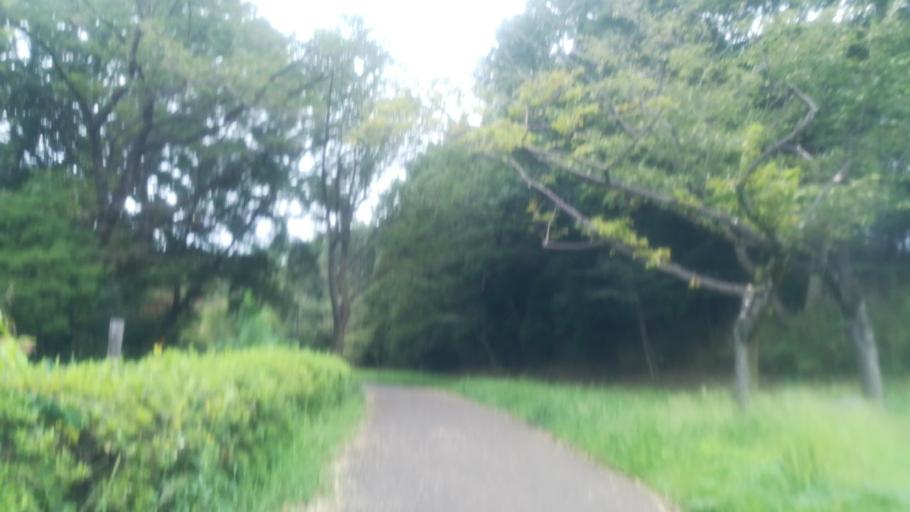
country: JP
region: Tokyo
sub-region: Machida-shi
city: Machida
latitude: 35.5881
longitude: 139.4000
